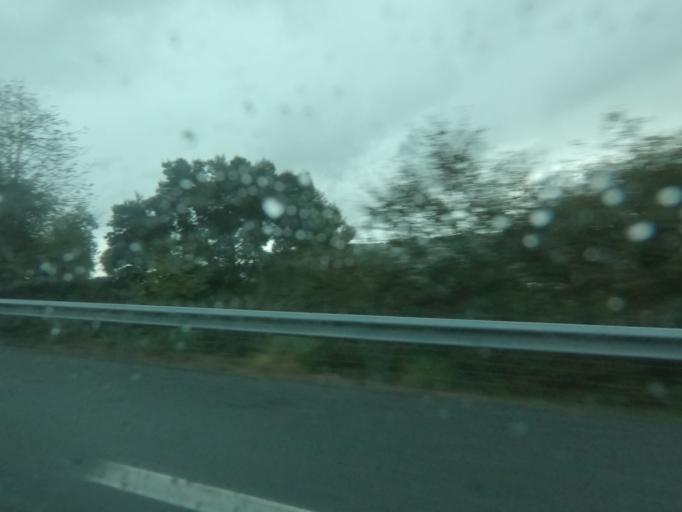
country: ES
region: Galicia
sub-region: Provincia de Pontevedra
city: Pontevedra
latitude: 42.3793
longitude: -8.6365
